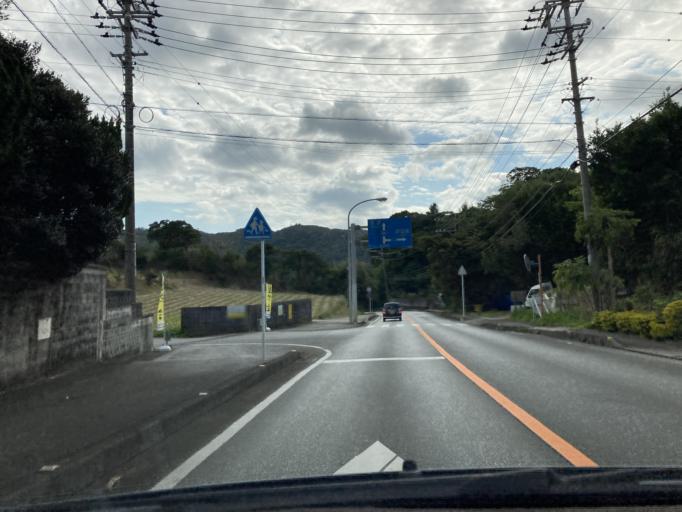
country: JP
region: Okinawa
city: Nago
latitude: 26.6558
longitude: 127.9835
